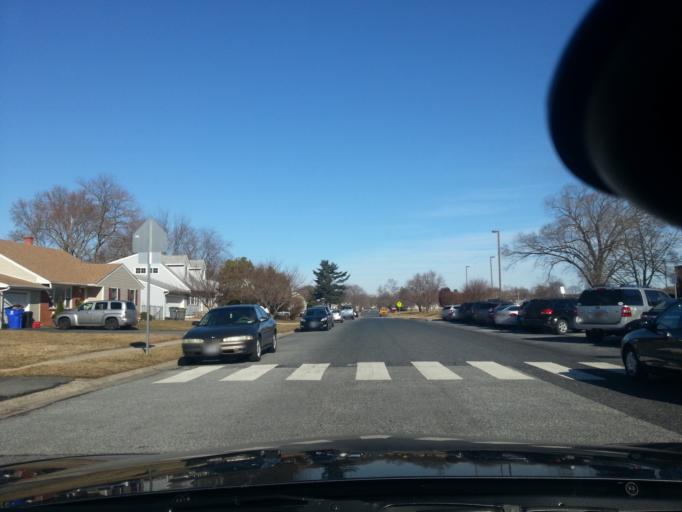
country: US
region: Delaware
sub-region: New Castle County
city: Brookside
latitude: 39.6717
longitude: -75.7112
